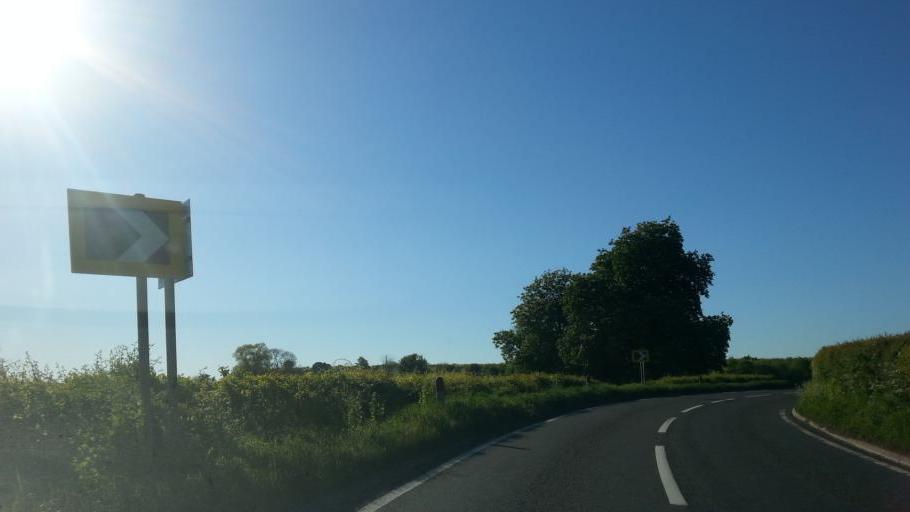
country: GB
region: England
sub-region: Somerset
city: Castle Cary
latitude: 51.0682
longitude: -2.4856
